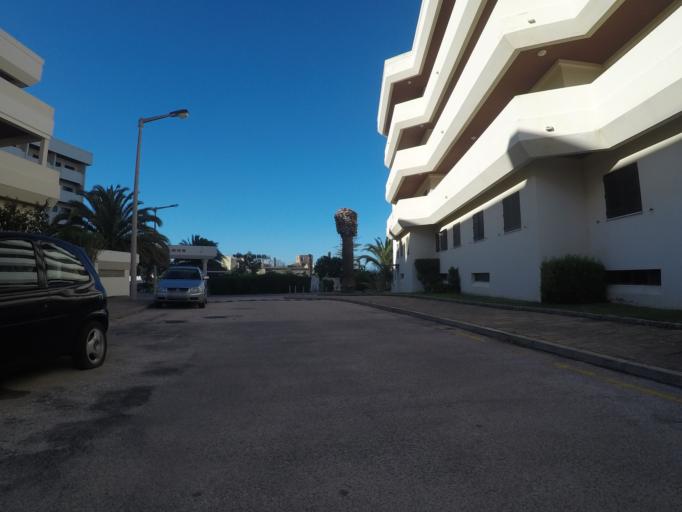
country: PT
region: Faro
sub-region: Lagos
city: Lagos
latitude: 37.0937
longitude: -8.6703
